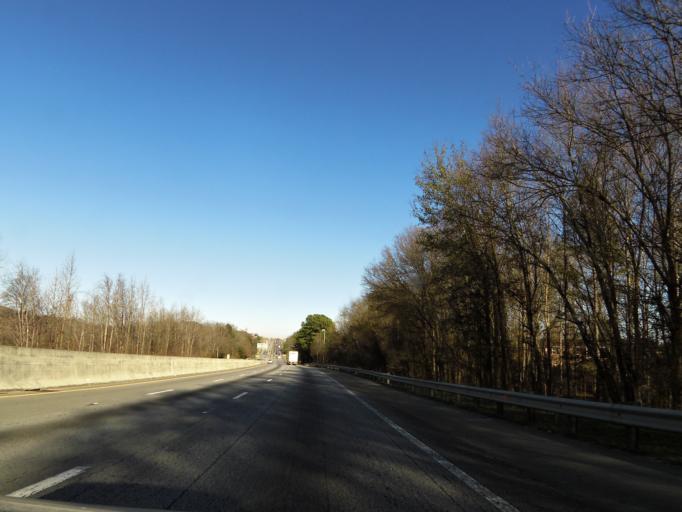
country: US
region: South Carolina
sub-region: Spartanburg County
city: Duncan
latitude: 34.9043
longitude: -82.1223
